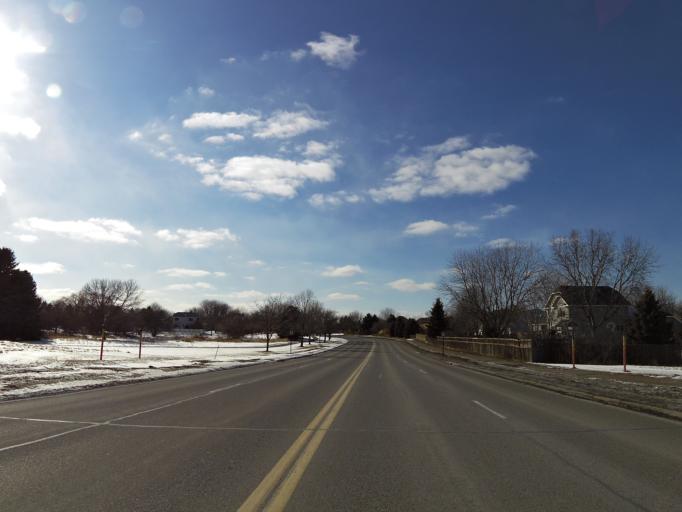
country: US
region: Minnesota
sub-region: Washington County
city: Woodbury
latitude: 44.9053
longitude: -92.9538
